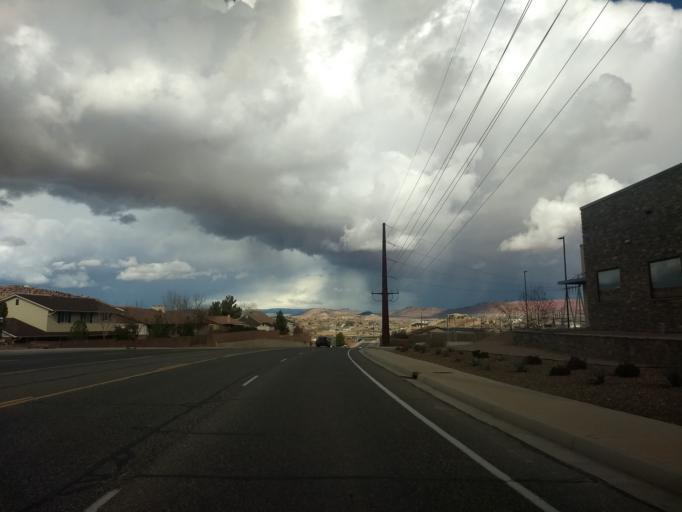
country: US
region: Utah
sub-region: Washington County
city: Saint George
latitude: 37.0570
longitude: -113.5505
